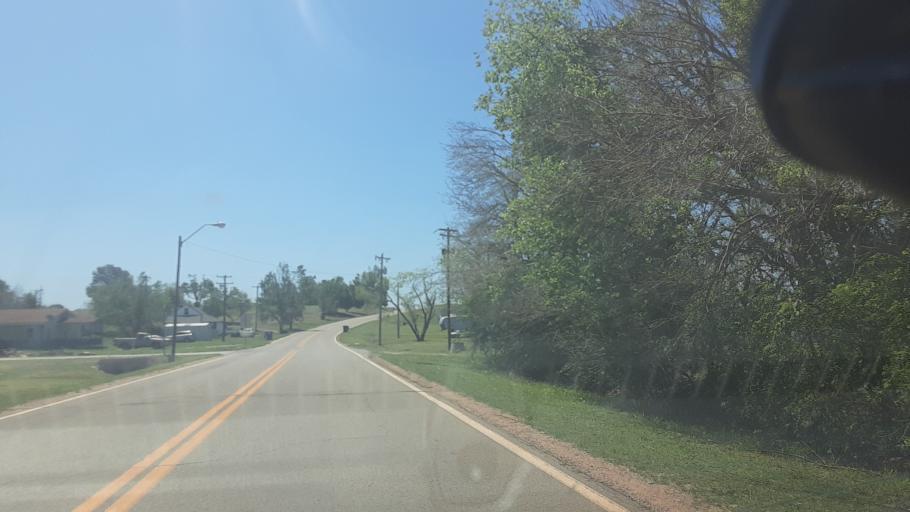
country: US
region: Oklahoma
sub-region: Logan County
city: Guthrie
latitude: 36.0631
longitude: -97.4073
